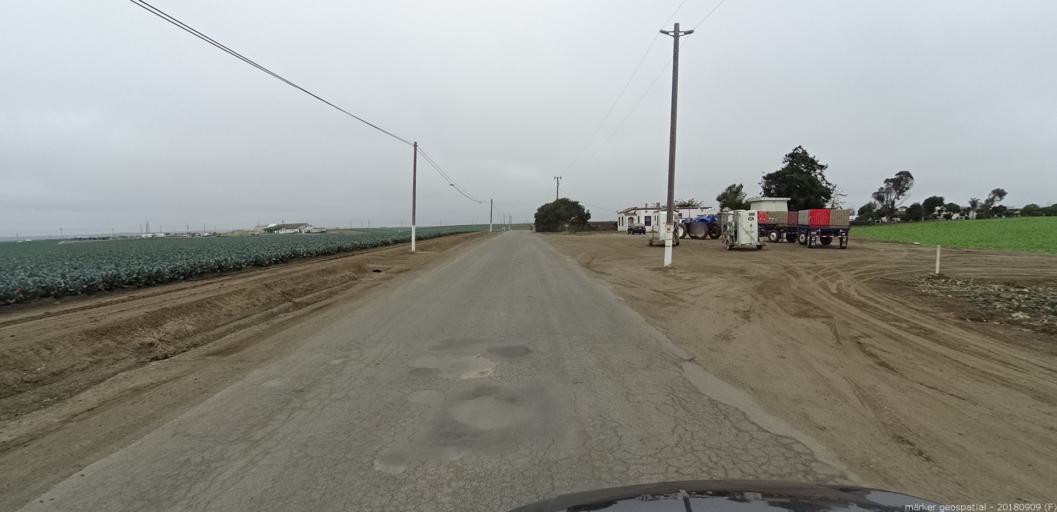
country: US
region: California
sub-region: Monterey County
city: Boronda
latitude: 36.7055
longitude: -121.6758
